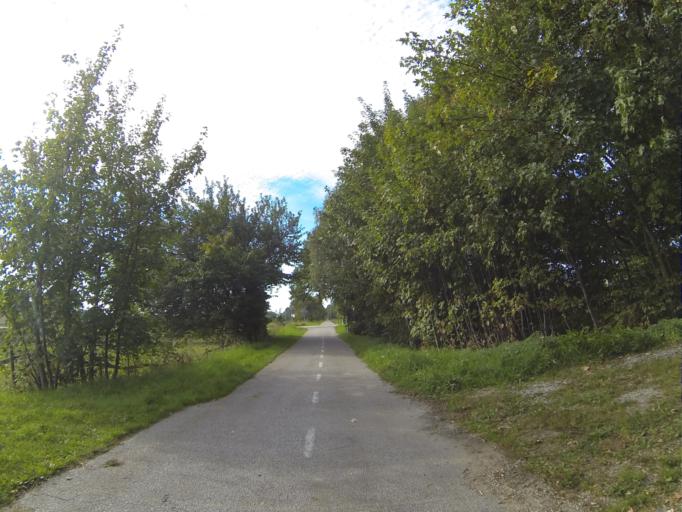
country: SE
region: Skane
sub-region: Lunds Kommun
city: Lund
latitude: 55.7134
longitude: 13.2984
